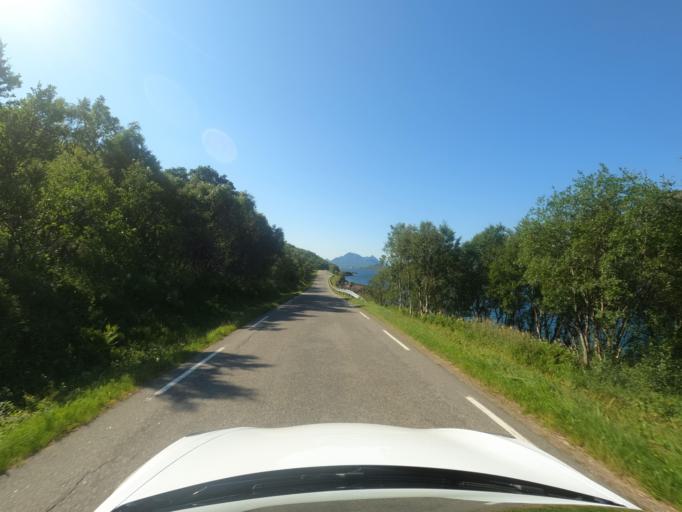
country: NO
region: Nordland
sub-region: Hadsel
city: Stokmarknes
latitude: 68.3795
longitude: 15.0861
